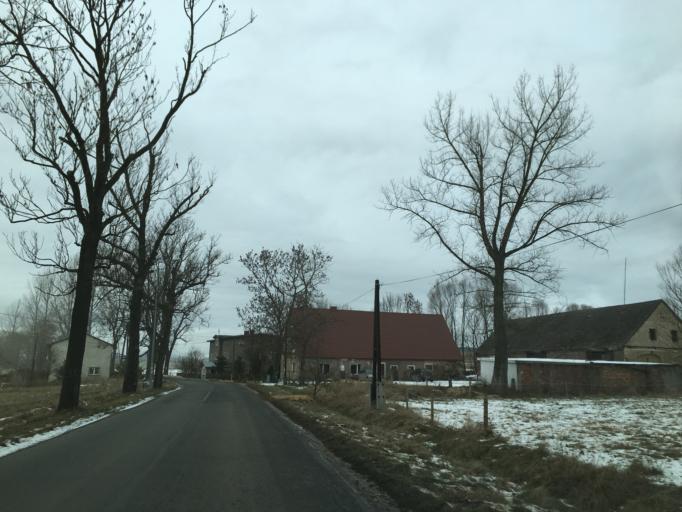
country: PL
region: Lower Silesian Voivodeship
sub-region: Powiat kamiennogorski
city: Krzeszow
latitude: 50.7071
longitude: 16.1119
